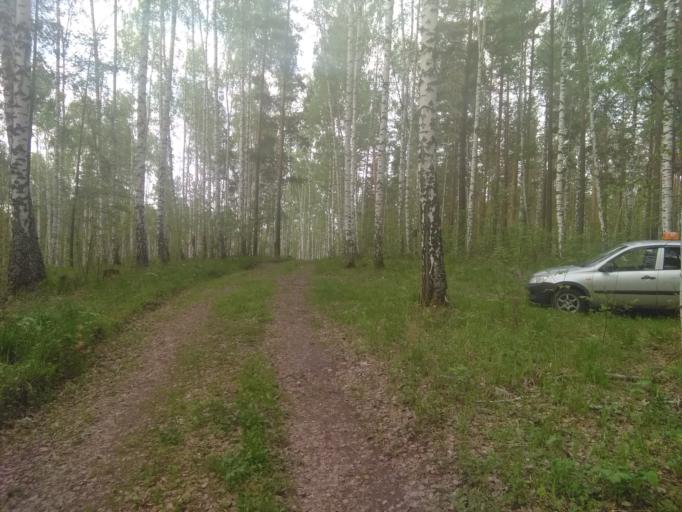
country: RU
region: Chelyabinsk
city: Miass
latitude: 55.1053
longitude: 60.0111
